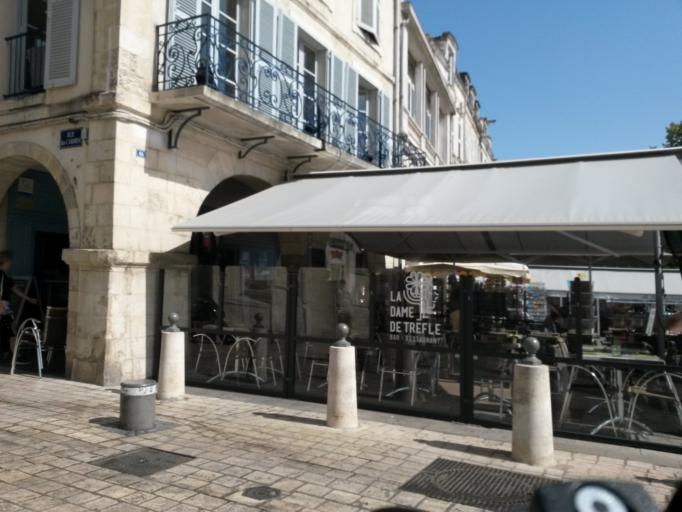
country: FR
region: Poitou-Charentes
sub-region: Departement de la Charente-Maritime
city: La Rochelle
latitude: 46.1567
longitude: -1.1545
